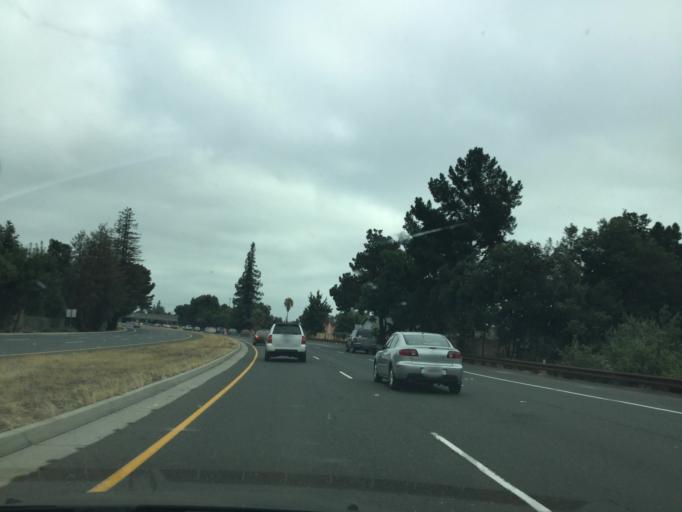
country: US
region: California
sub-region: Santa Clara County
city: Campbell
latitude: 37.3112
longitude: -121.9630
